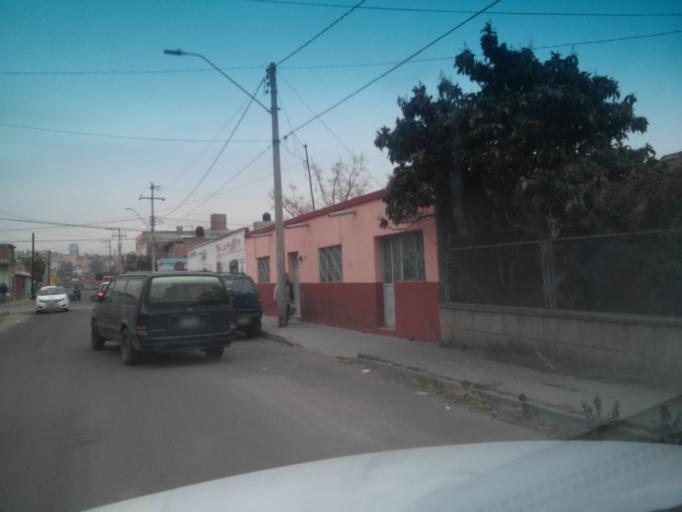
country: MX
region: Durango
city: Victoria de Durango
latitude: 24.0373
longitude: -104.6835
